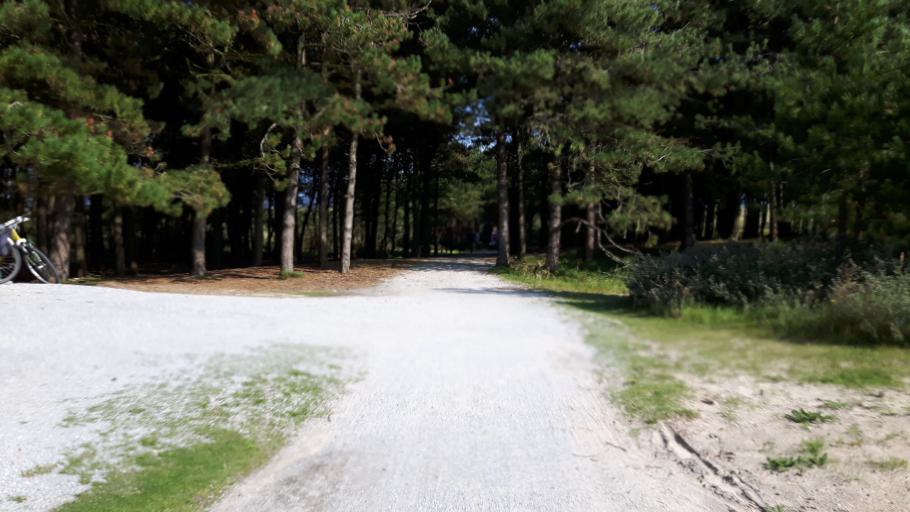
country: NL
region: Friesland
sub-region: Gemeente Ameland
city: Nes
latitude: 53.4589
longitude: 5.8152
